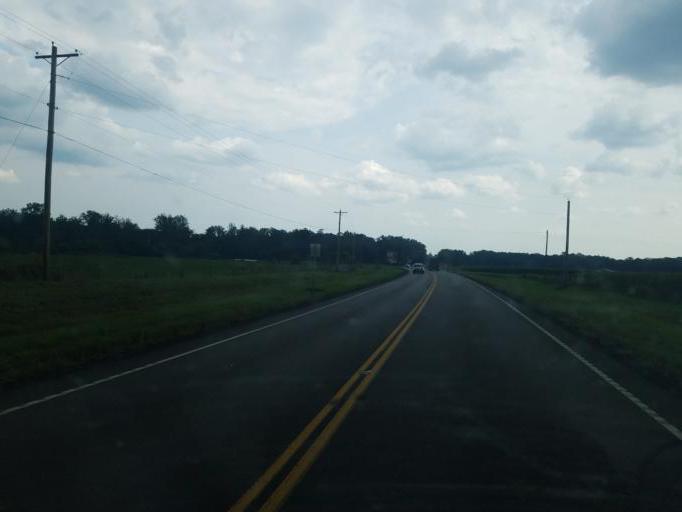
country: US
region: Ohio
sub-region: Knox County
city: Mount Vernon
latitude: 40.4271
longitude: -82.5093
